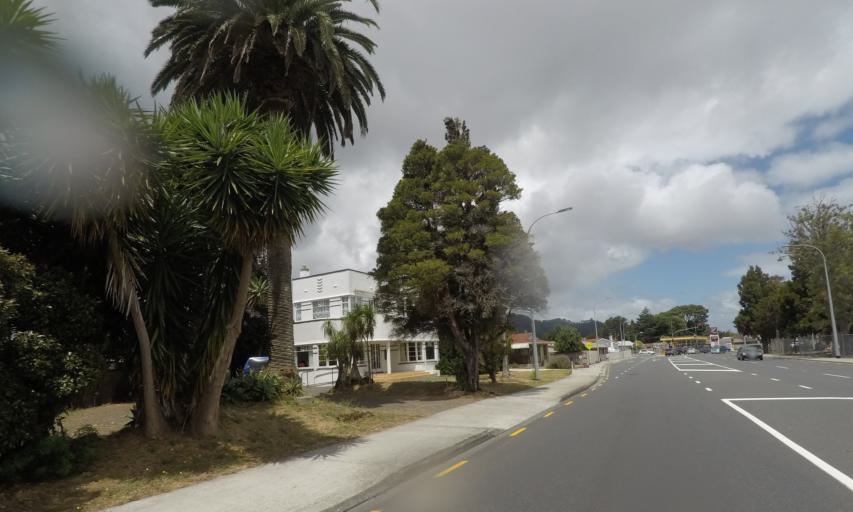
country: NZ
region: Northland
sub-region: Whangarei
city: Whangarei
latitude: -35.7073
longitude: 174.3209
